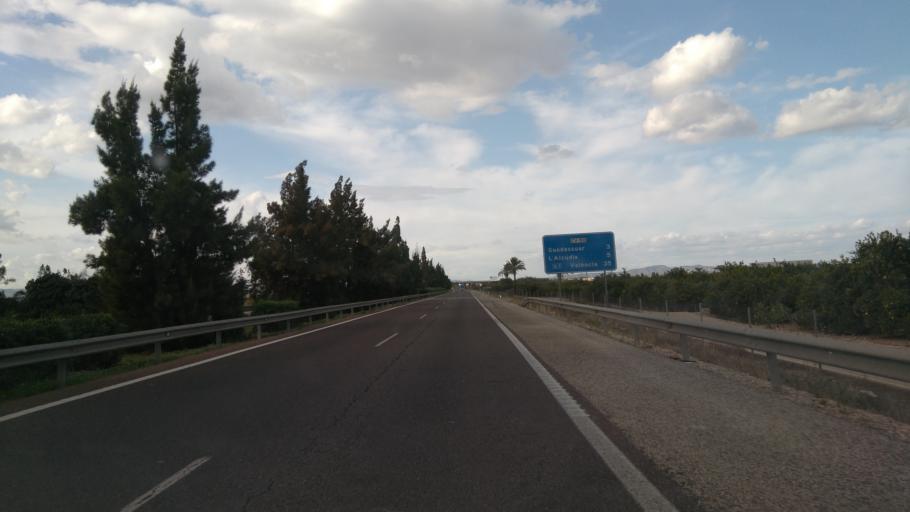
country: ES
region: Valencia
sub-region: Provincia de Valencia
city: Guadassuar
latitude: 39.1658
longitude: -0.4594
